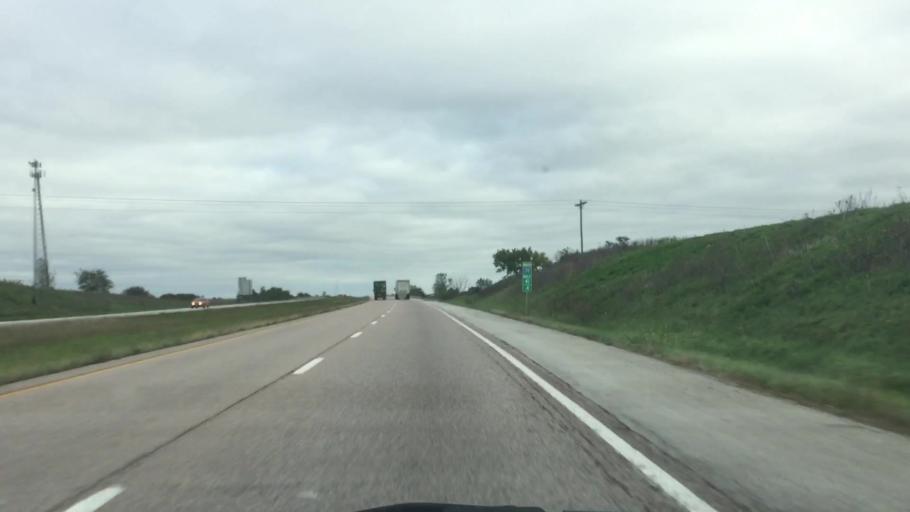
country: US
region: Missouri
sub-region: Clinton County
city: Lathrop
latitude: 39.5708
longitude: -94.2620
